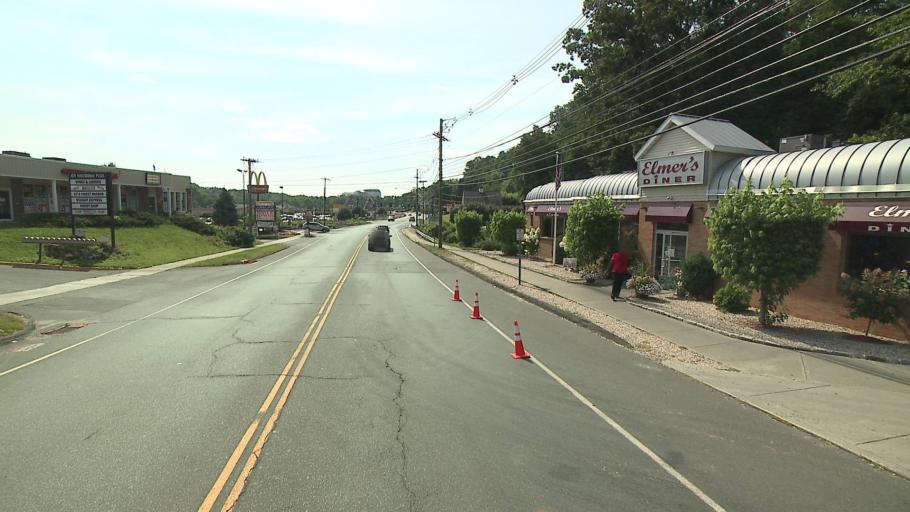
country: US
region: Connecticut
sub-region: Fairfield County
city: Danbury
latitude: 41.4144
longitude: -73.4595
